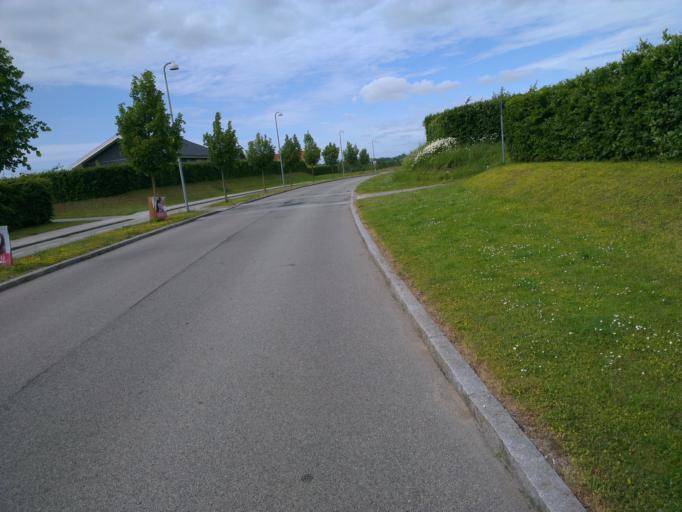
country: DK
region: Capital Region
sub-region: Frederikssund Kommune
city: Frederikssund
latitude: 55.8643
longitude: 12.0733
